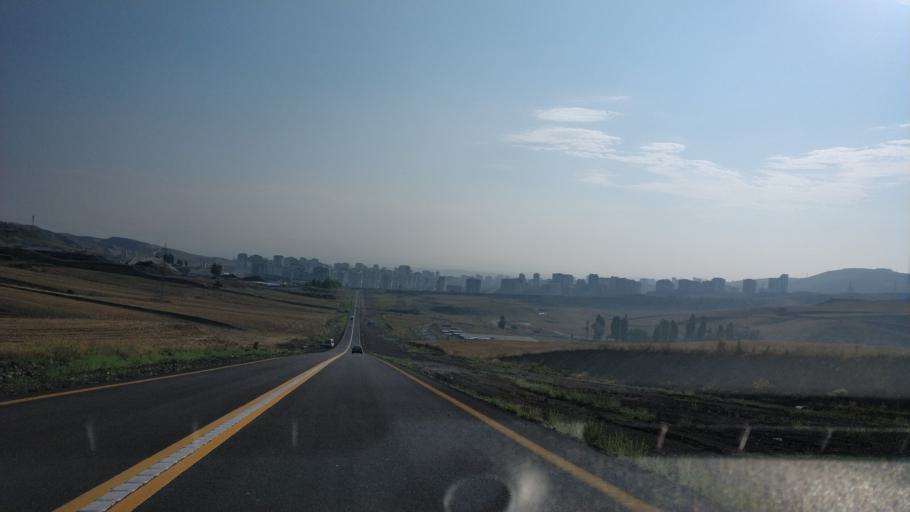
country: TR
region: Ankara
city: Etimesgut
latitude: 39.8775
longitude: 32.6009
